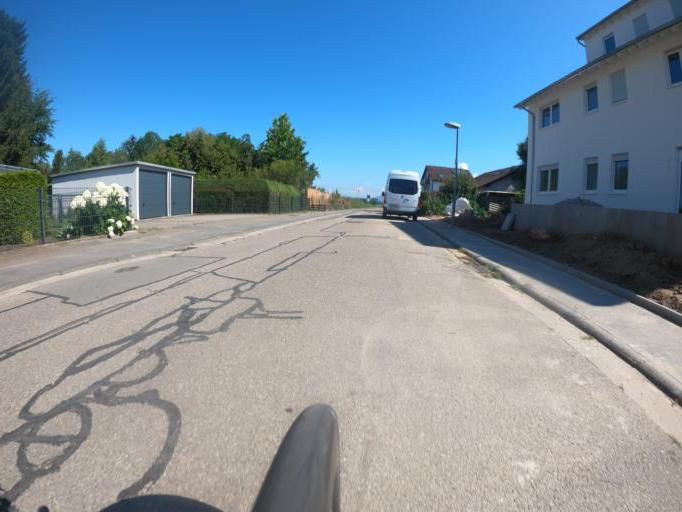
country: DE
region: Baden-Wuerttemberg
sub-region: Karlsruhe Region
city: Sandhausen
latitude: 49.3493
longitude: 8.6668
